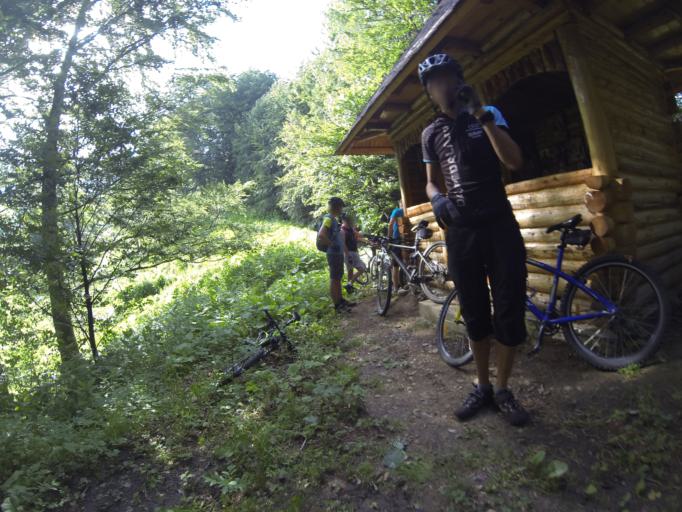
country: RO
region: Valcea
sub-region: Comuna Barbatesti
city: Barbatesti
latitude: 45.2625
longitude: 24.1493
